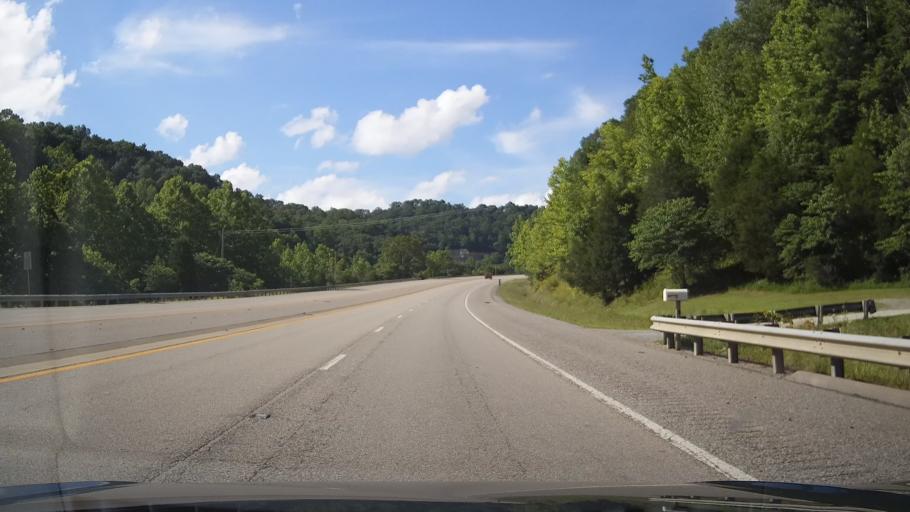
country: US
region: Kentucky
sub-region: Lawrence County
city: Louisa
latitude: 38.0265
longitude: -82.6524
